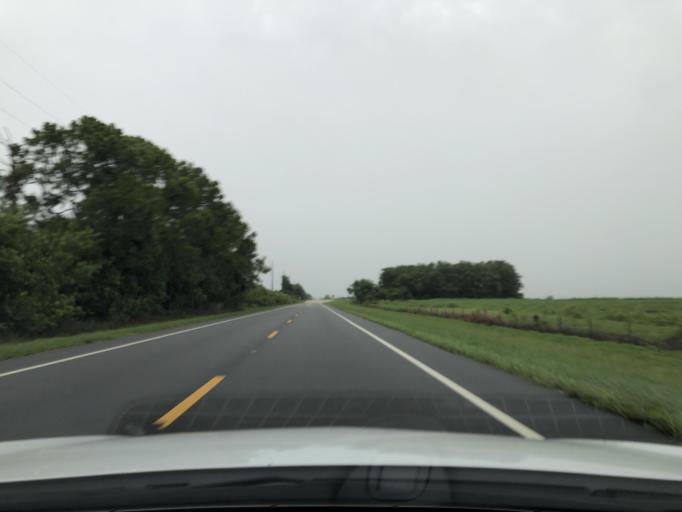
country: US
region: Florida
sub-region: Collier County
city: Immokalee
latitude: 26.2948
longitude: -81.4210
